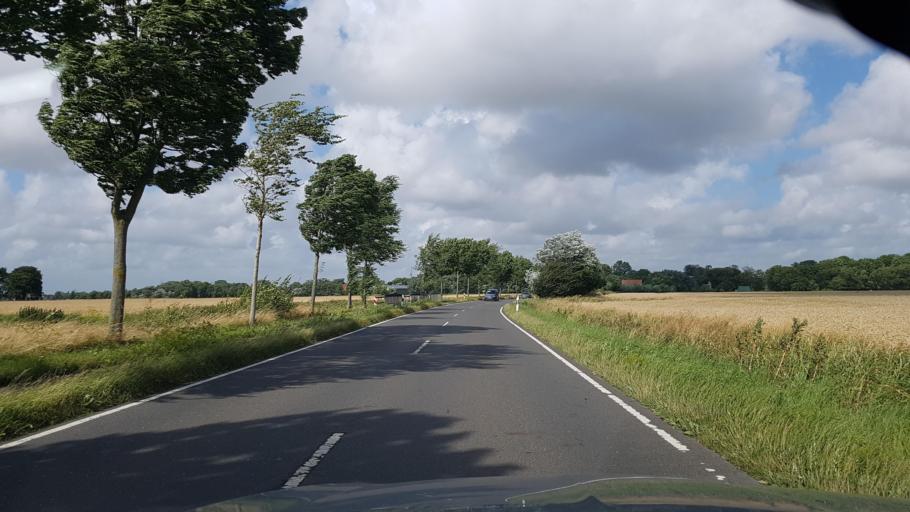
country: DE
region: Schleswig-Holstein
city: Suderdeich
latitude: 54.1958
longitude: 8.9034
